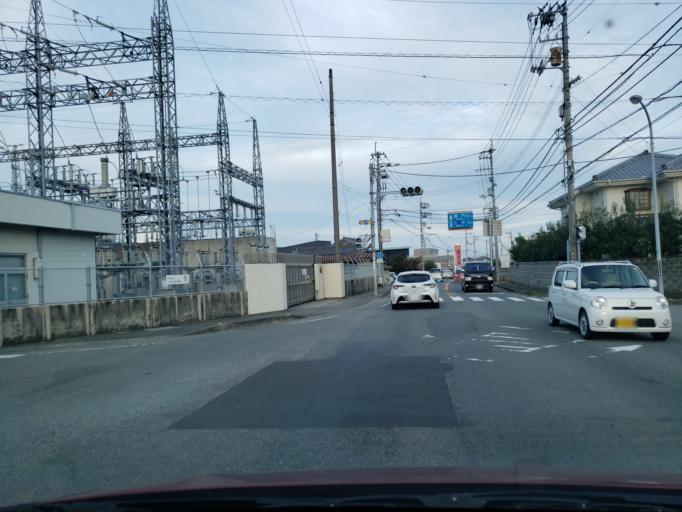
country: JP
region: Tokushima
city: Kamojimacho-jogejima
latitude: 34.0934
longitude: 134.3088
